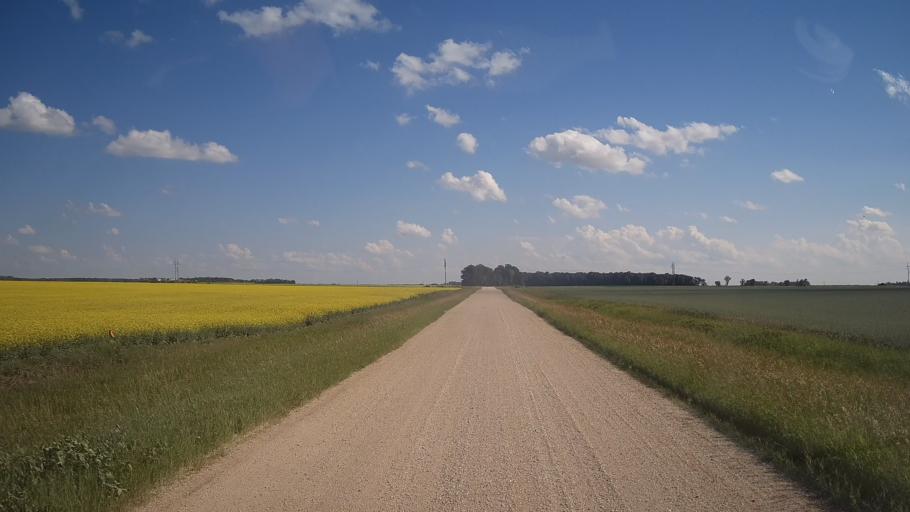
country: CA
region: Manitoba
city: Stonewall
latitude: 50.1269
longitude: -97.5054
